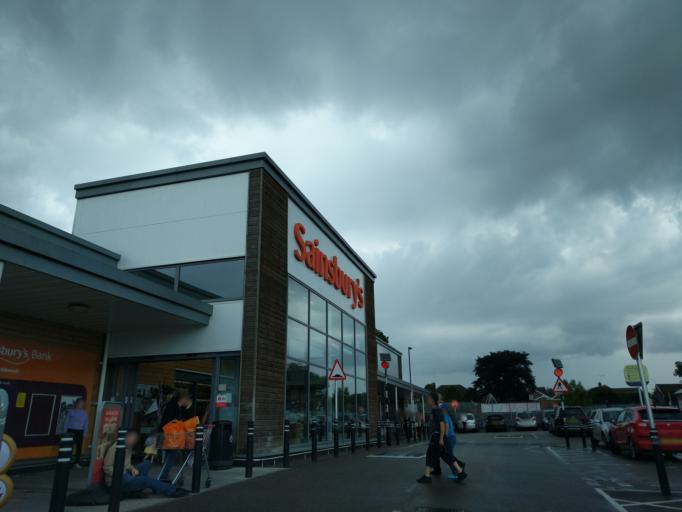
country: GB
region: England
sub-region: Suffolk
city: Lakenheath
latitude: 52.3423
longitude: 0.5134
